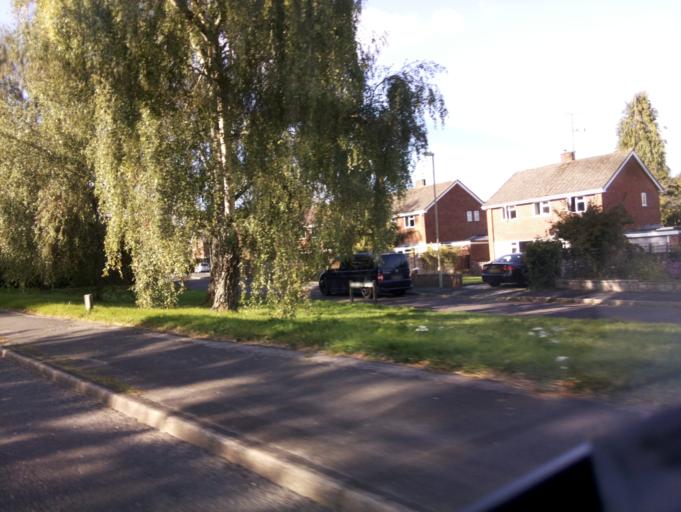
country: GB
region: England
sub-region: Hampshire
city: Alton
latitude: 51.1428
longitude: -0.9880
